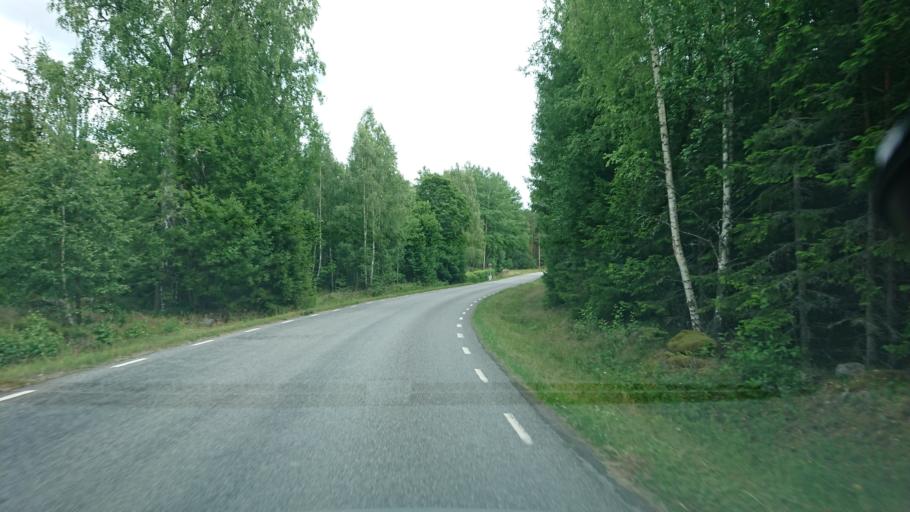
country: SE
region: Uppsala
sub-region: Osthammars Kommun
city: Bjorklinge
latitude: 60.0055
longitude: 17.4509
